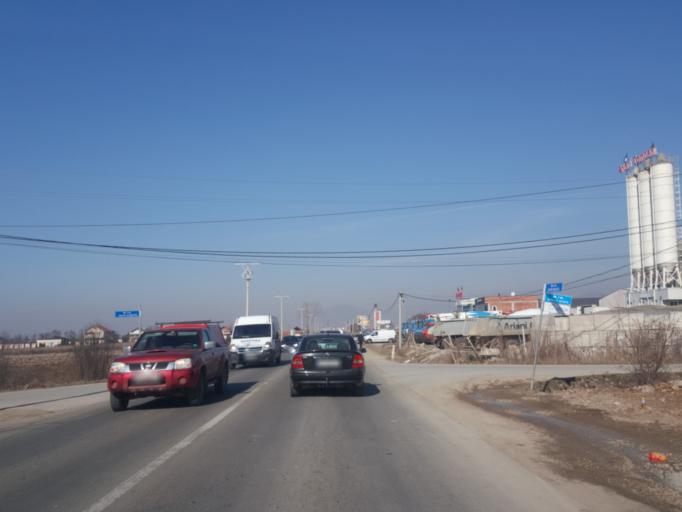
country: XK
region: Mitrovica
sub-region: Vushtrri
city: Vushtrri
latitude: 42.7994
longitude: 20.9964
